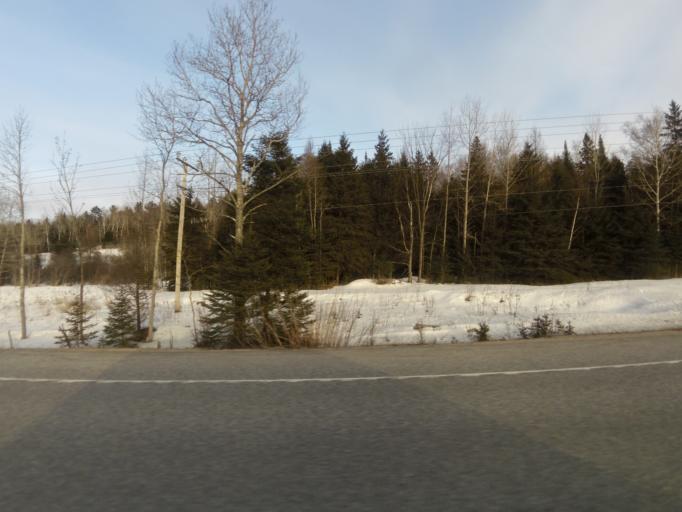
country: CA
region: Quebec
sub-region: Outaouais
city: Wakefield
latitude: 45.9039
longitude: -76.0261
